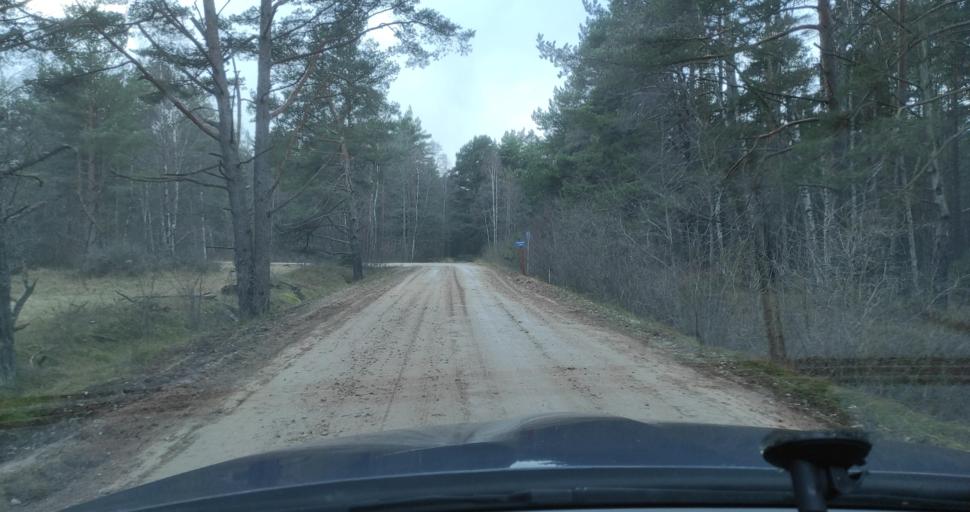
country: LV
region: Pavilostas
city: Pavilosta
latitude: 56.8370
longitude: 21.0760
